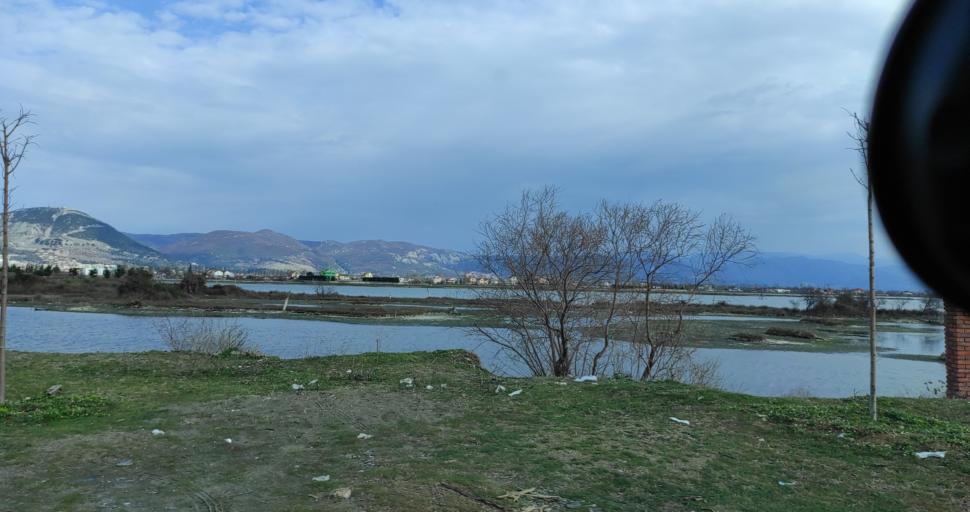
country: AL
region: Lezhe
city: Shengjin
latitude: 41.7701
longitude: 19.6004
